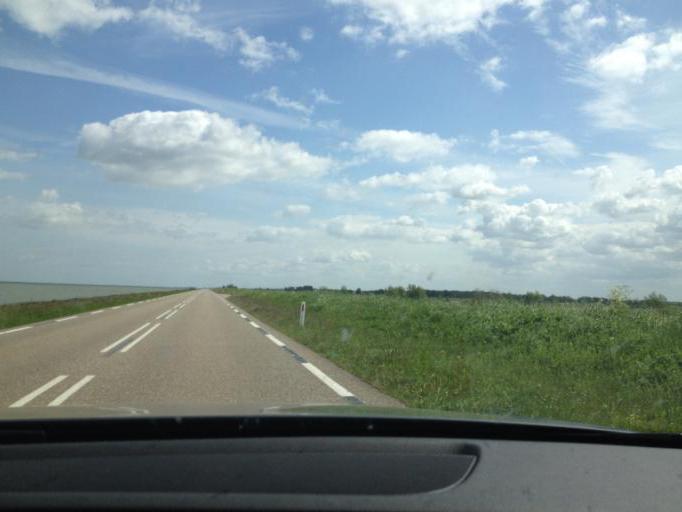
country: NL
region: Flevoland
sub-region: Gemeente Almere
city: Almere Stad
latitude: 52.4079
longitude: 5.1844
